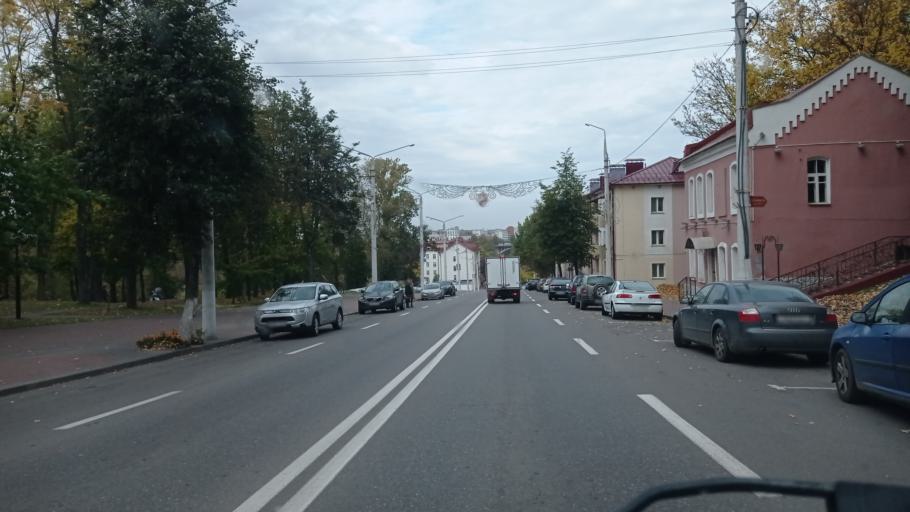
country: BY
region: Vitebsk
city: Vitebsk
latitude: 55.1859
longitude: 30.2023
